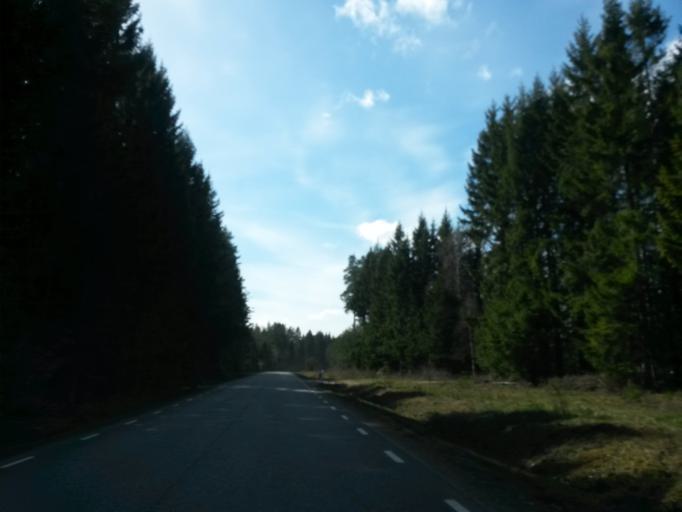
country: SE
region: Vaestra Goetaland
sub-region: Vargarda Kommun
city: Jonstorp
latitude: 57.9834
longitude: 12.7362
